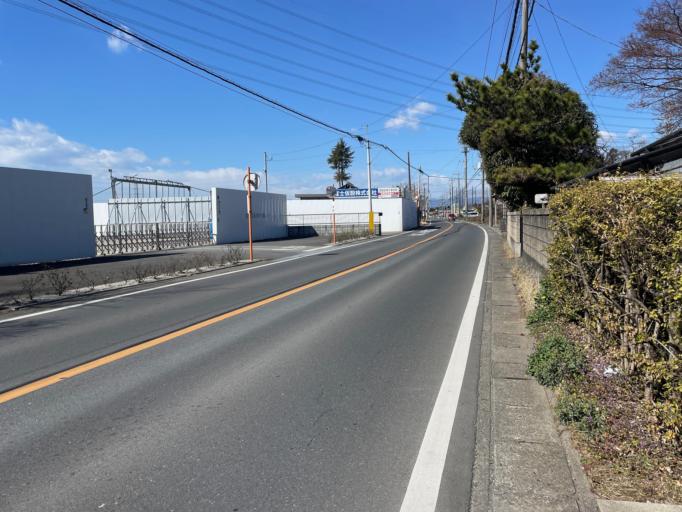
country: JP
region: Saitama
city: Kawagoe
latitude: 35.9483
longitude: 139.4469
